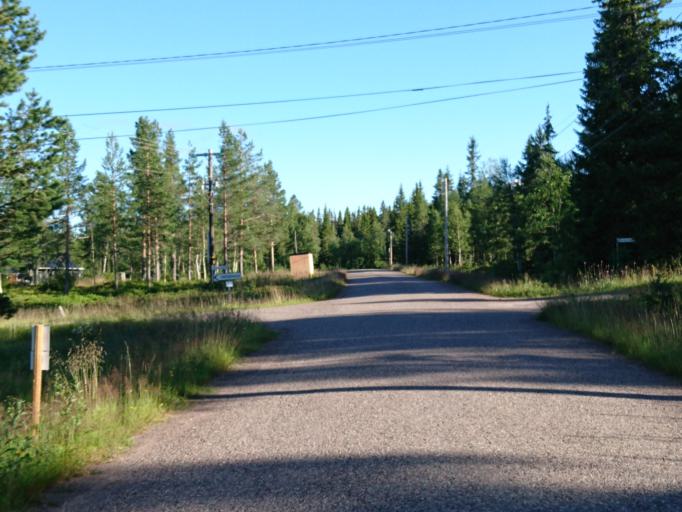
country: SE
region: Dalarna
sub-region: Malung-Saelens kommun
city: Malung
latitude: 61.1720
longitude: 13.1760
